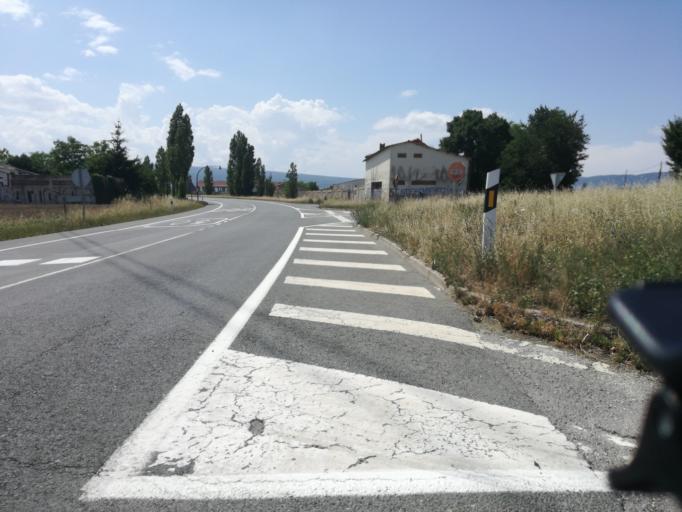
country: ES
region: Basque Country
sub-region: Provincia de Alava
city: Gasteiz / Vitoria
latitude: 42.8622
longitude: -2.7317
